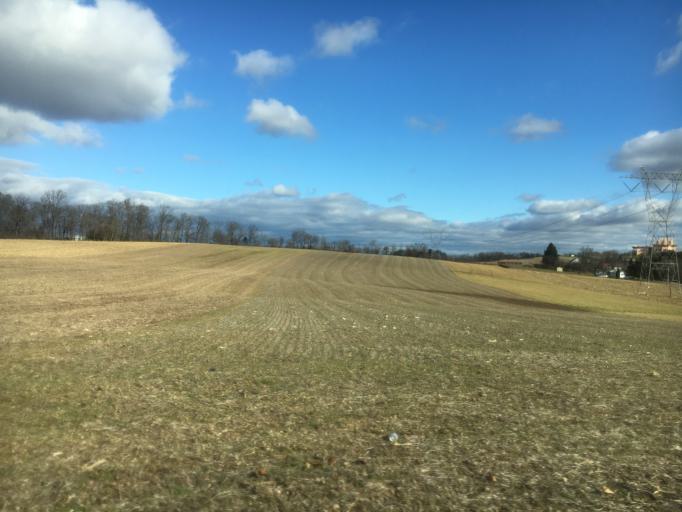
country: US
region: Pennsylvania
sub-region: Lehigh County
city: Egypt
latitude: 40.6943
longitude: -75.5629
